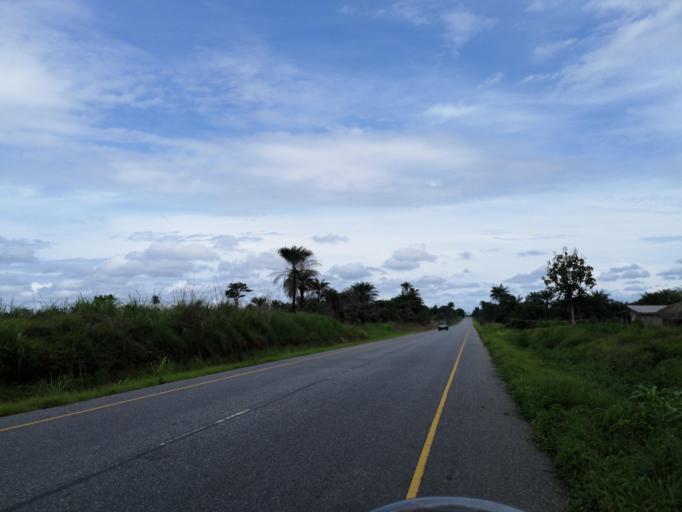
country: SL
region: Northern Province
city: Port Loko
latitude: 8.7410
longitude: -12.9405
